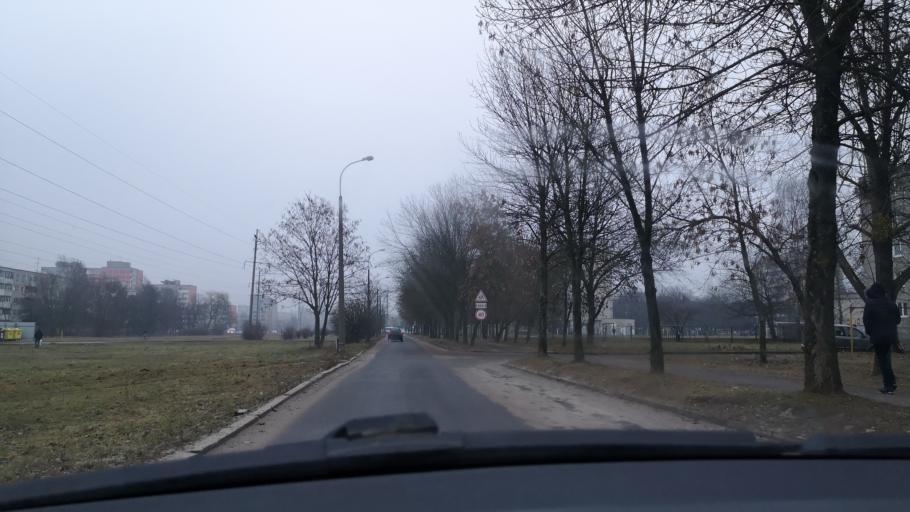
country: BY
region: Brest
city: Brest
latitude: 52.1035
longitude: 23.7573
